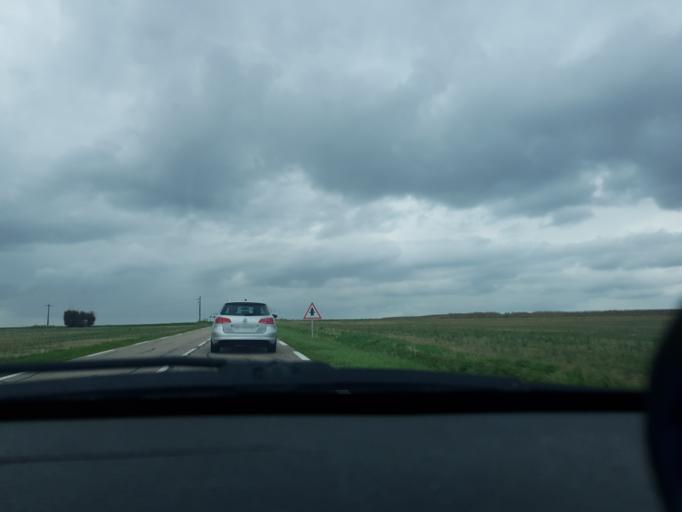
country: FR
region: Lorraine
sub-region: Departement de la Moselle
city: Faulquemont
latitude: 48.9945
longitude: 6.5979
